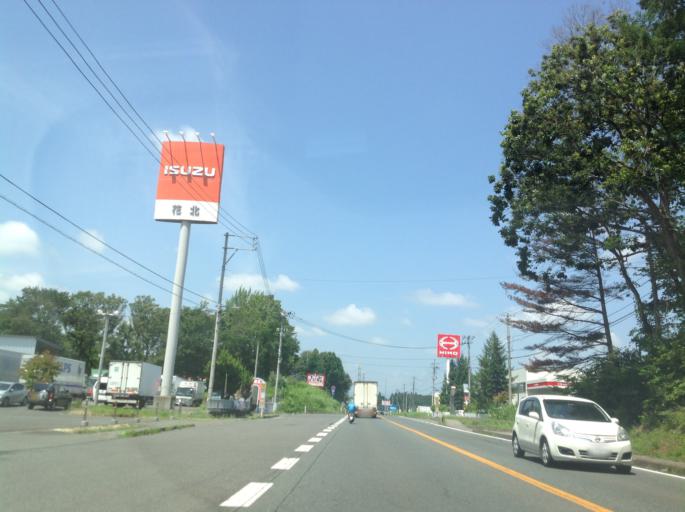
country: JP
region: Iwate
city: Hanamaki
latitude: 39.3415
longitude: 141.1077
